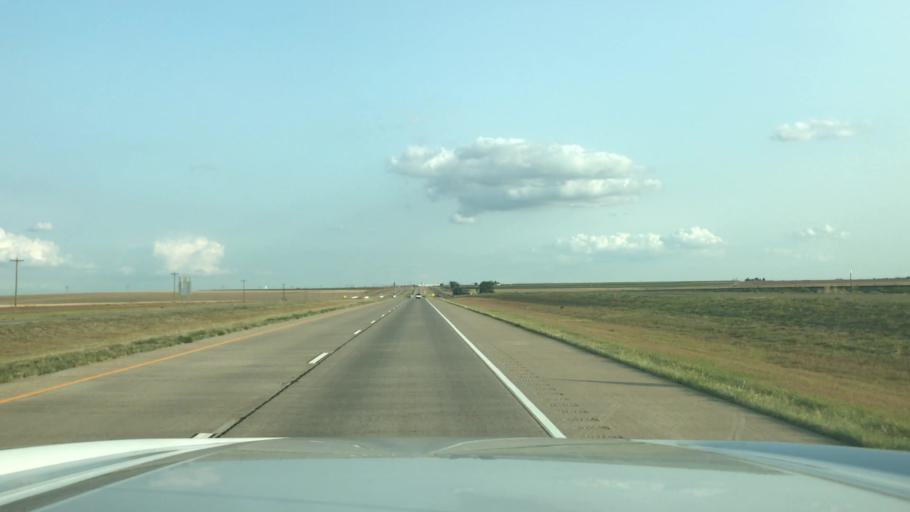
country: US
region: Texas
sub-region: Swisher County
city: Tulia
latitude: 34.6148
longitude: -101.8118
